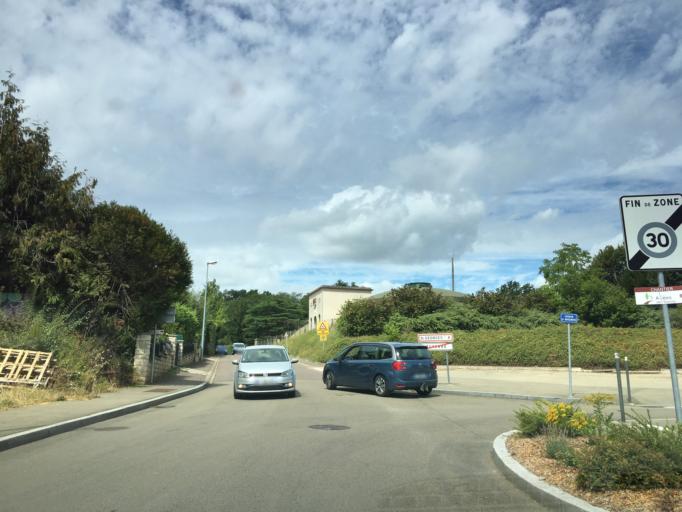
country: FR
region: Bourgogne
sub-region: Departement de l'Yonne
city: Saint-Georges-sur-Baulche
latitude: 47.8008
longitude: 3.5482
